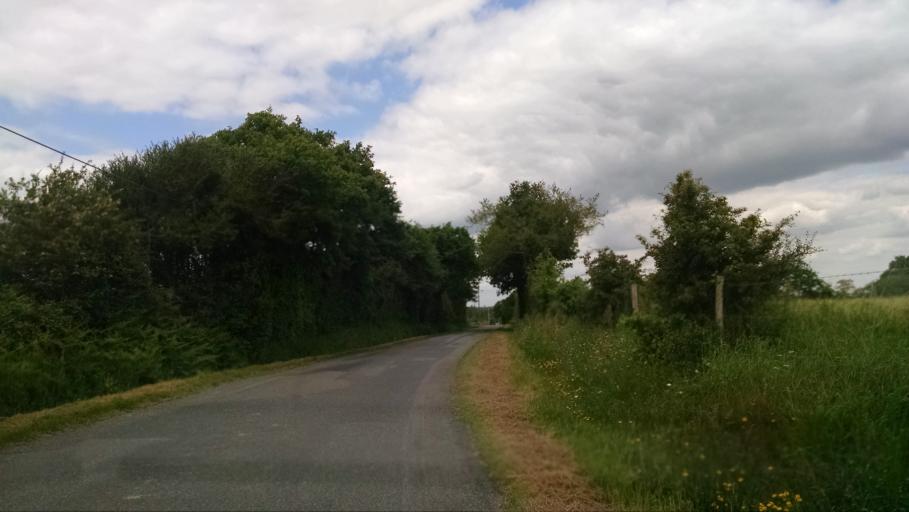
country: FR
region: Pays de la Loire
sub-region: Departement de la Loire-Atlantique
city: Remouille
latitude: 47.0222
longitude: -1.3825
